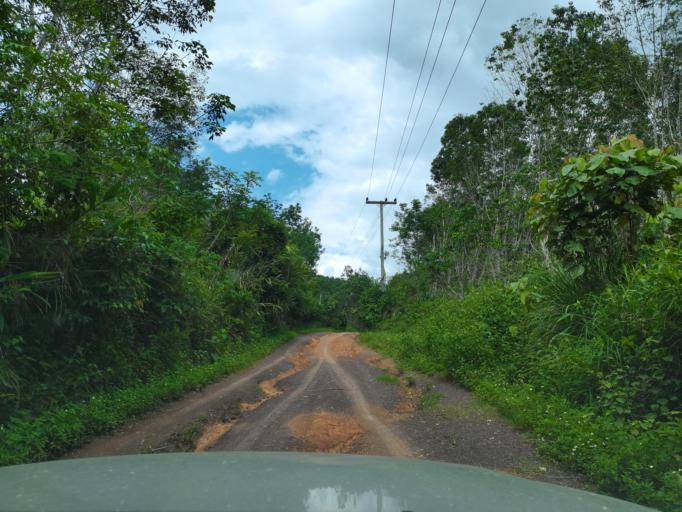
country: LA
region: Loungnamtha
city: Muang Long
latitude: 20.7006
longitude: 101.0230
